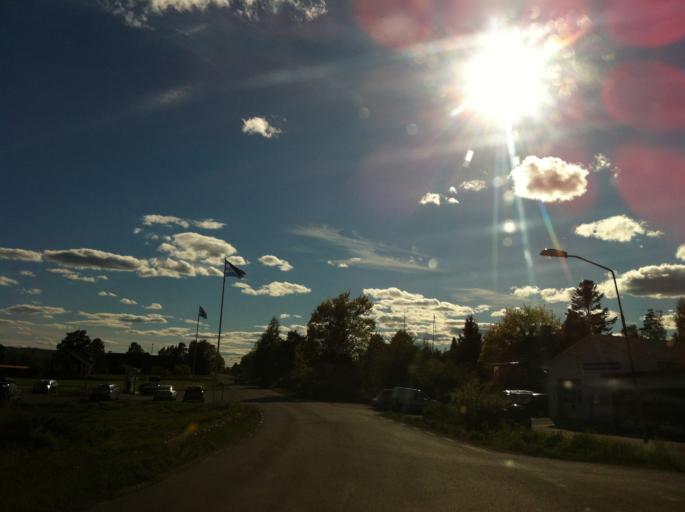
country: SE
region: Dalarna
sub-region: Leksand Municipality
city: Siljansnas
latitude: 60.7724
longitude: 14.8823
